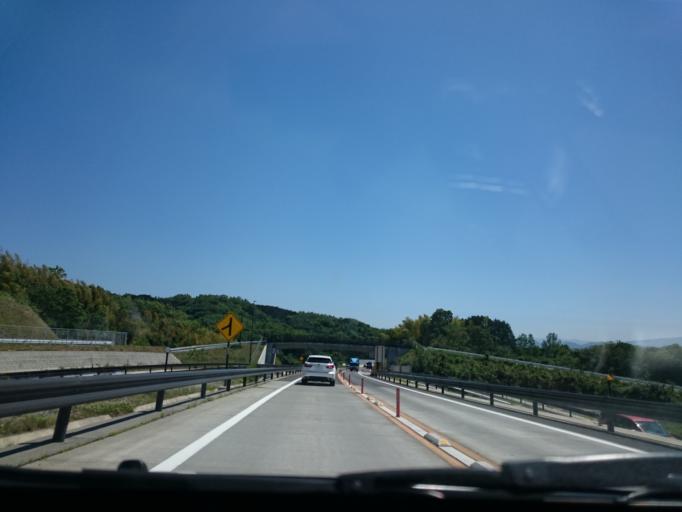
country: JP
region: Shizuoka
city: Mishima
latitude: 35.1203
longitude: 138.9495
